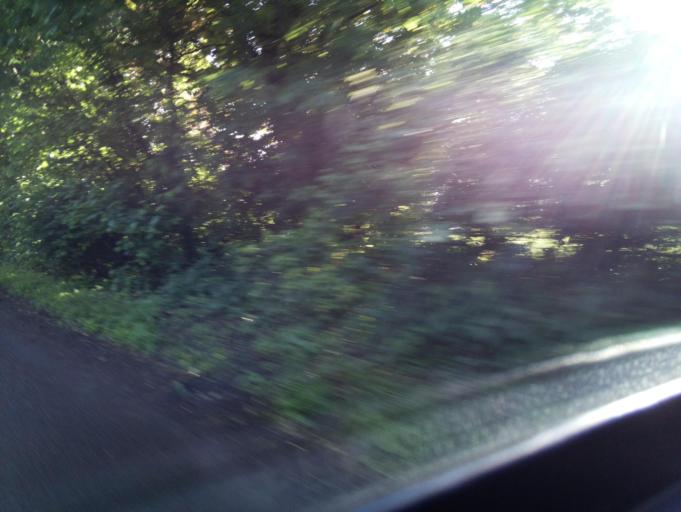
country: GB
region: England
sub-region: Lincolnshire
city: Navenby
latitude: 53.0819
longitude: -0.6301
